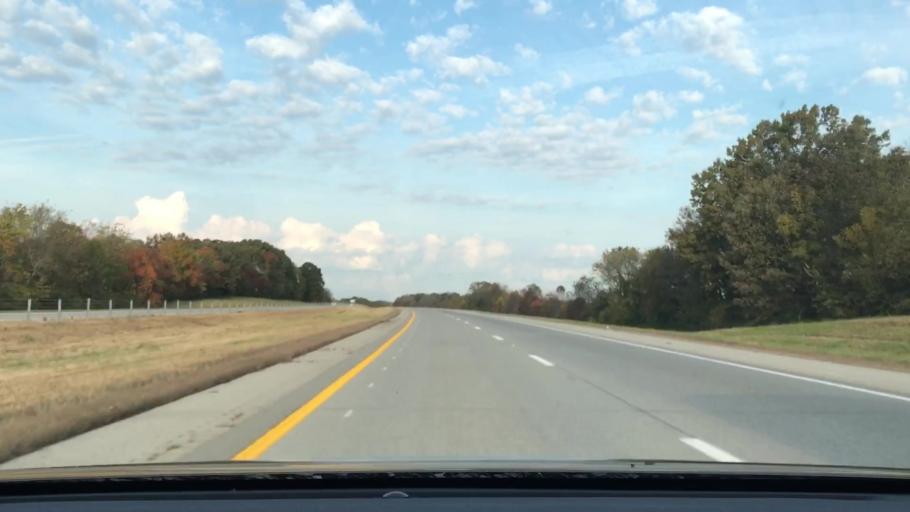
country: US
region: Kentucky
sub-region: Trigg County
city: Cadiz
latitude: 36.8459
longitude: -87.6802
